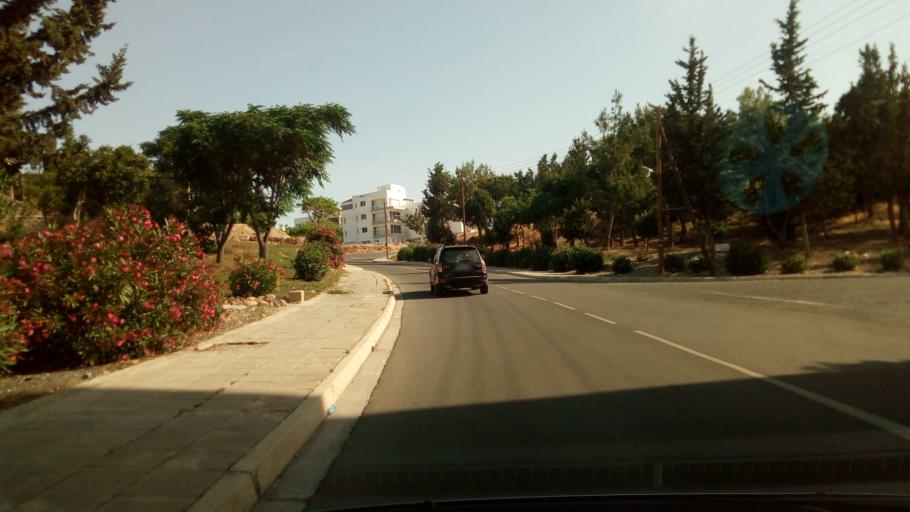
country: CY
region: Pafos
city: Paphos
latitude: 34.7633
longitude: 32.4366
